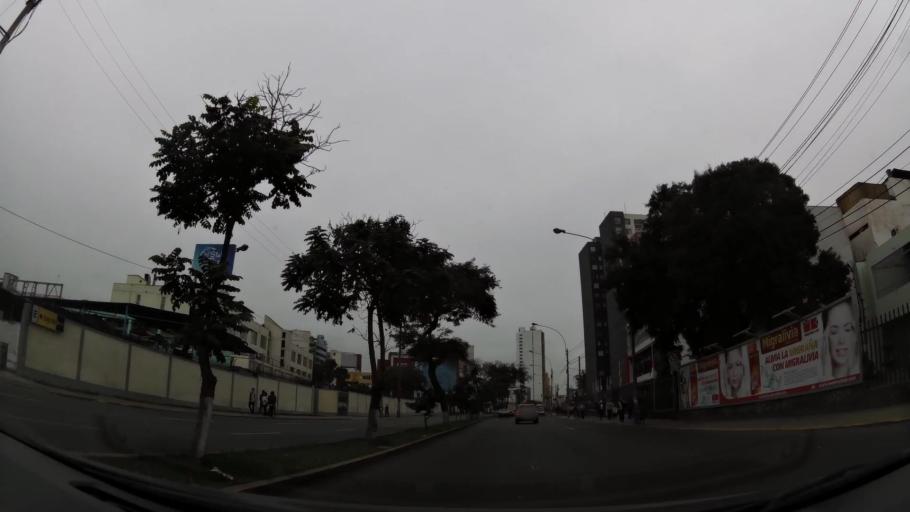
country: PE
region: Lima
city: Lima
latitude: -12.0717
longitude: -77.0602
